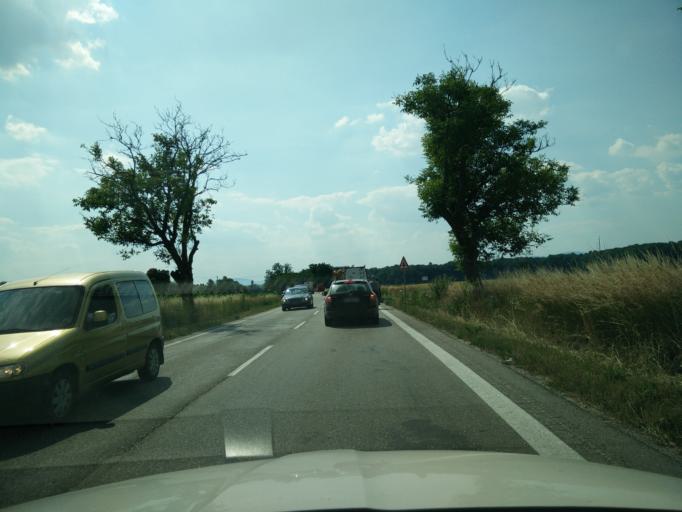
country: SK
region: Nitriansky
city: Banovce nad Bebravou
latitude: 48.6156
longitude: 18.2770
